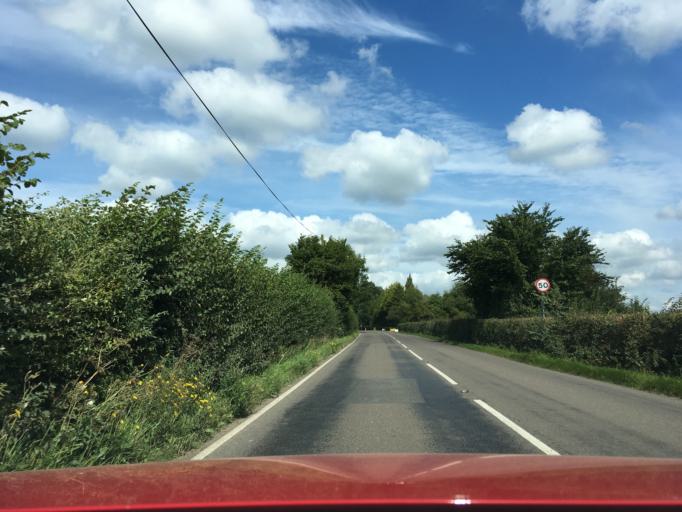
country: GB
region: England
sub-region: South Gloucestershire
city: Tytherington
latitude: 51.5960
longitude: -2.4436
